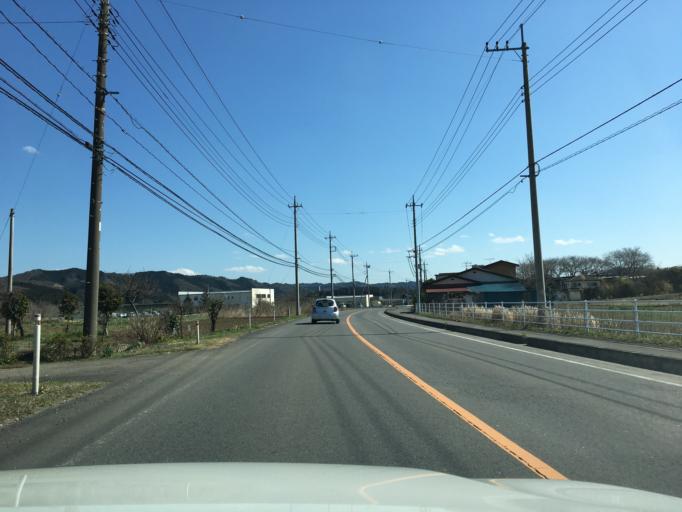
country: JP
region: Tochigi
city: Karasuyama
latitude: 36.7243
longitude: 140.1451
